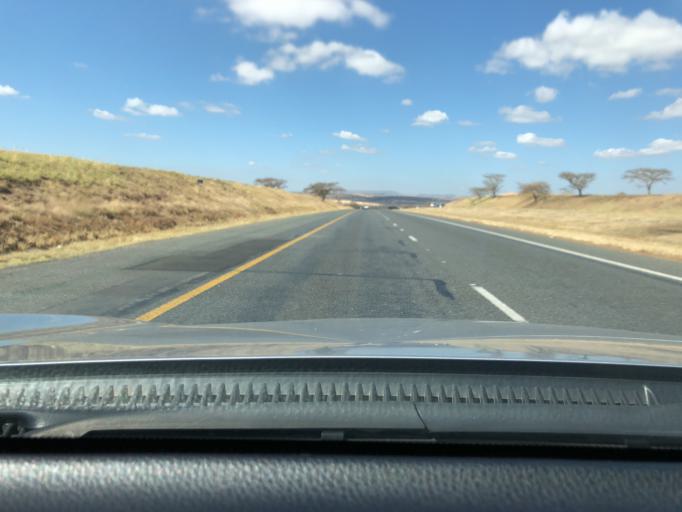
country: ZA
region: KwaZulu-Natal
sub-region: uThukela District Municipality
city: Estcourt
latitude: -28.9344
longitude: 29.7859
